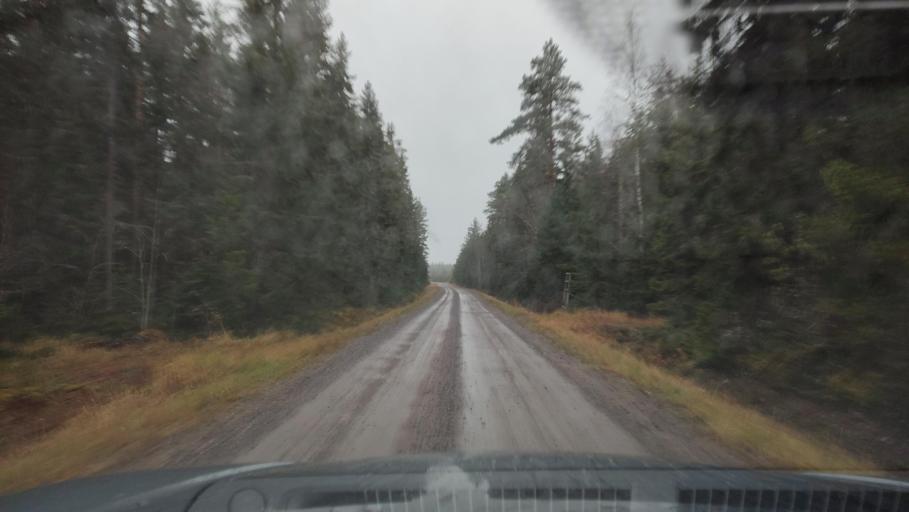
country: FI
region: Southern Ostrobothnia
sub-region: Suupohja
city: Karijoki
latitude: 62.2203
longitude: 21.7427
